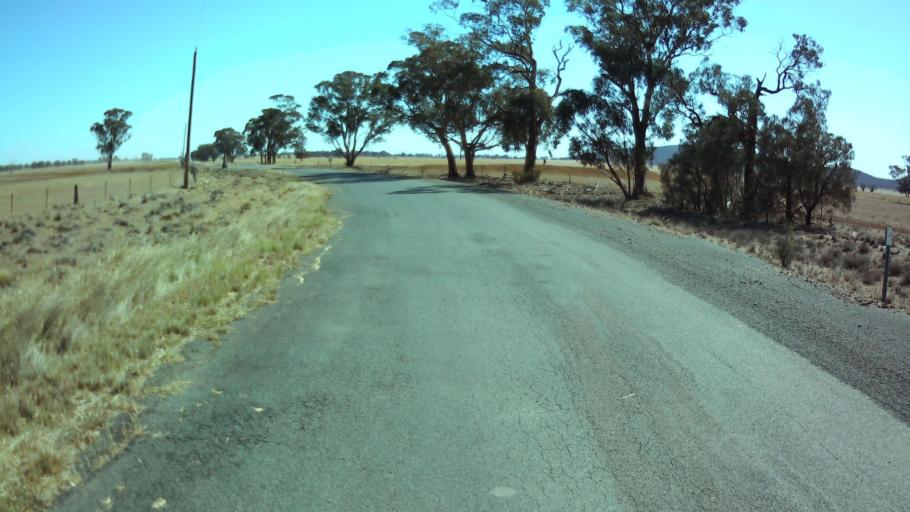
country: AU
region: New South Wales
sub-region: Weddin
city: Grenfell
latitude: -33.7050
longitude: 147.9180
